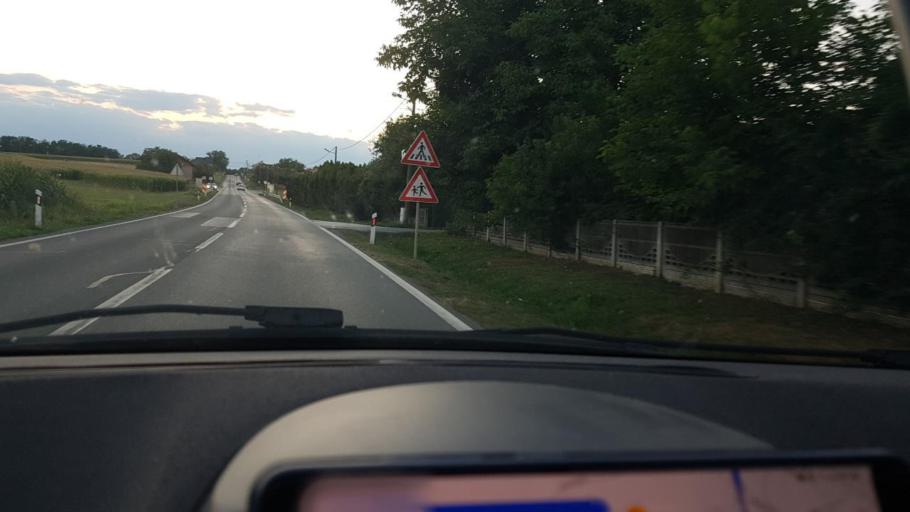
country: HR
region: Bjelovarsko-Bilogorska
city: Zdralovi
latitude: 45.8703
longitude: 16.9015
